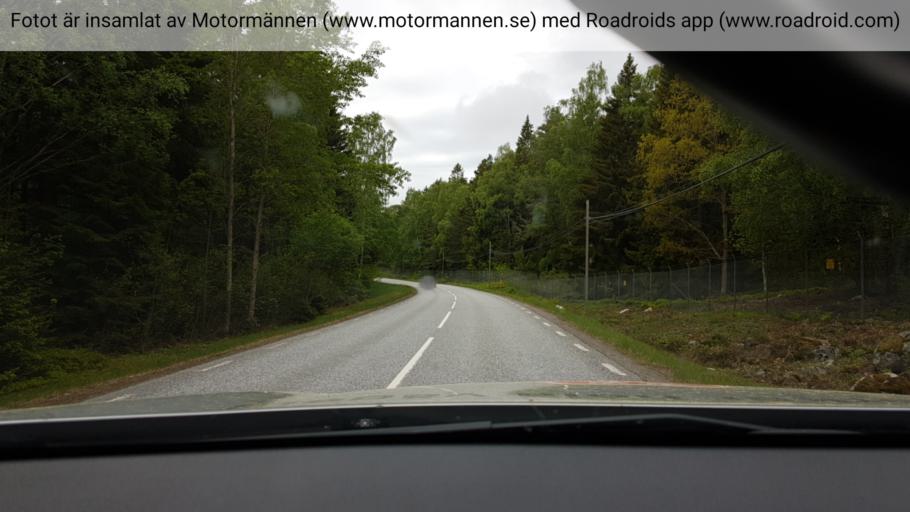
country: SE
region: Stockholm
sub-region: Nynashamns Kommun
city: Nynashamn
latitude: 58.9804
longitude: 18.0854
